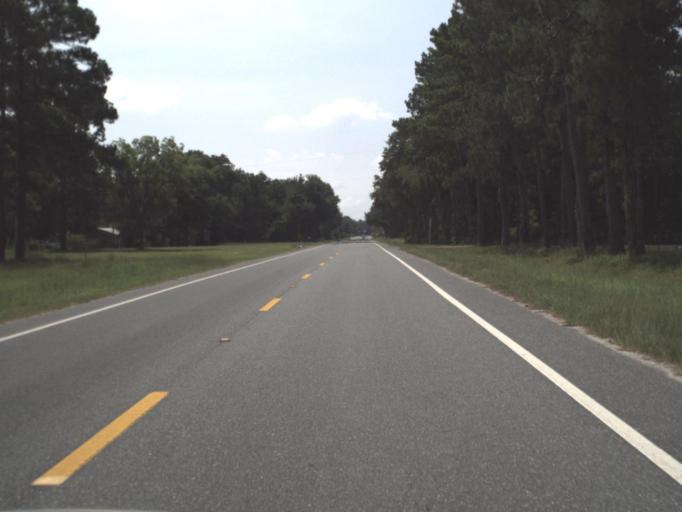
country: US
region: Georgia
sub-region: Echols County
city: Statenville
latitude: 30.6094
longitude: -83.1064
